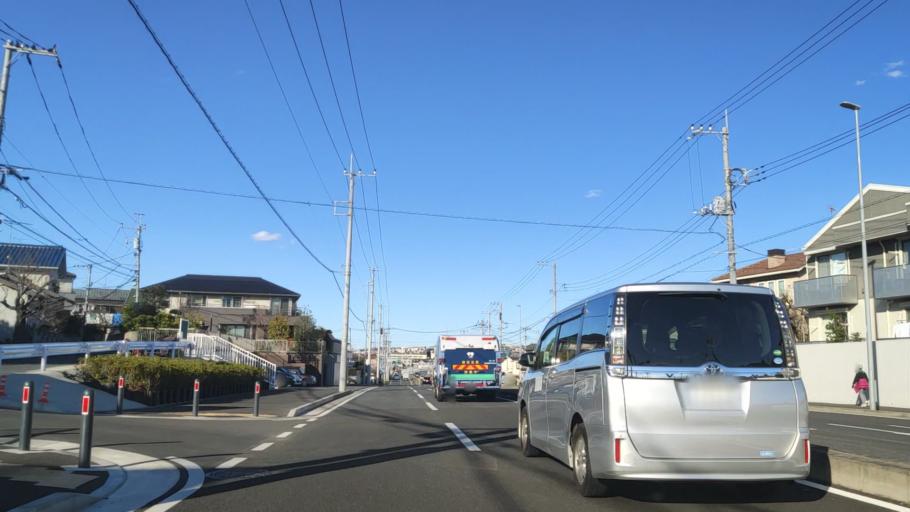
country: JP
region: Tokyo
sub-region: Machida-shi
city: Machida
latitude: 35.5205
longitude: 139.5445
